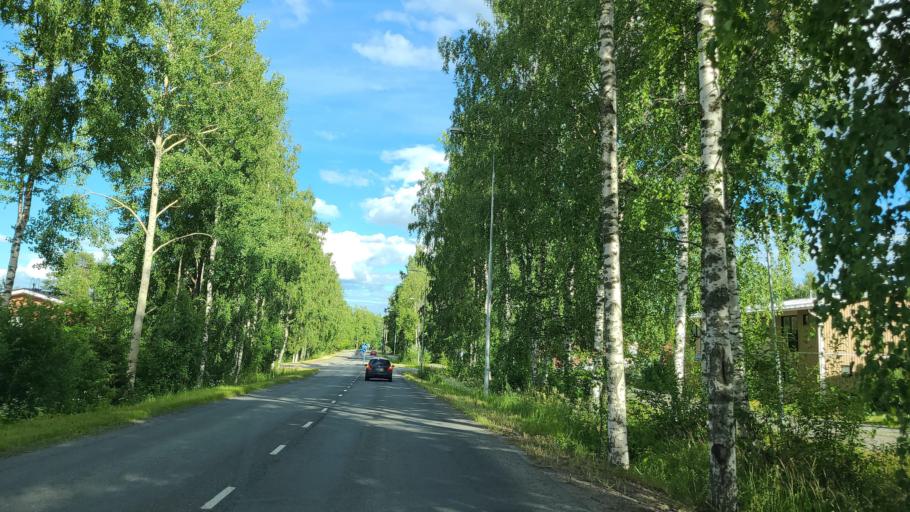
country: FI
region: Northern Savo
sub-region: Kuopio
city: Kuopio
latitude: 62.9378
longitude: 27.6508
